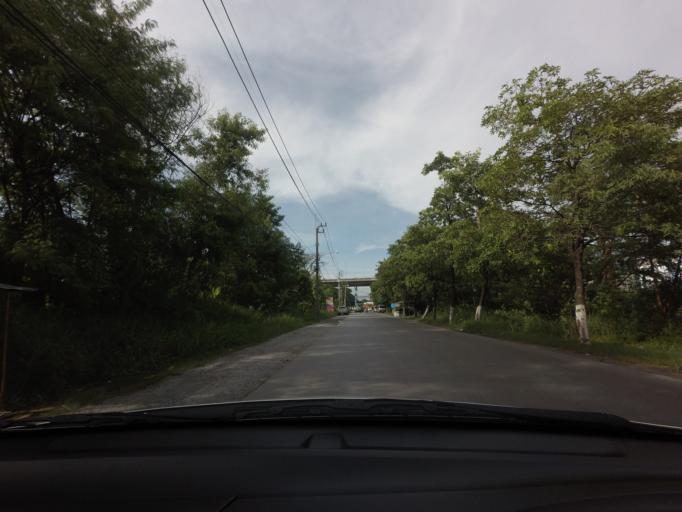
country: TH
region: Bangkok
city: Bang Na
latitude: 13.6601
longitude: 100.6601
